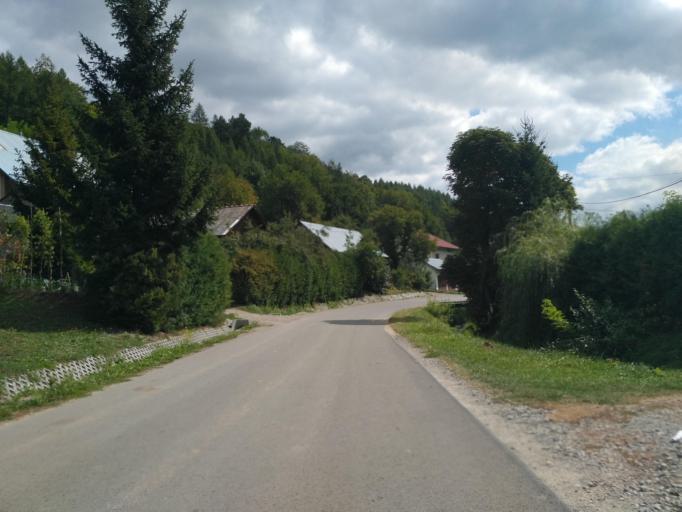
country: PL
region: Subcarpathian Voivodeship
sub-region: Powiat rzeszowski
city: Dynow
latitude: 49.7764
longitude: 22.2397
